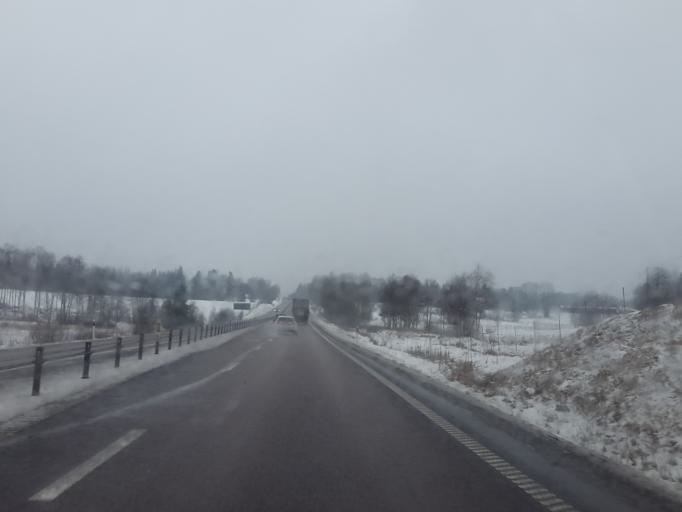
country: SE
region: Vaestra Goetaland
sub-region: Ulricehamns Kommun
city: Ulricehamn
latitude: 57.7970
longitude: 13.5926
